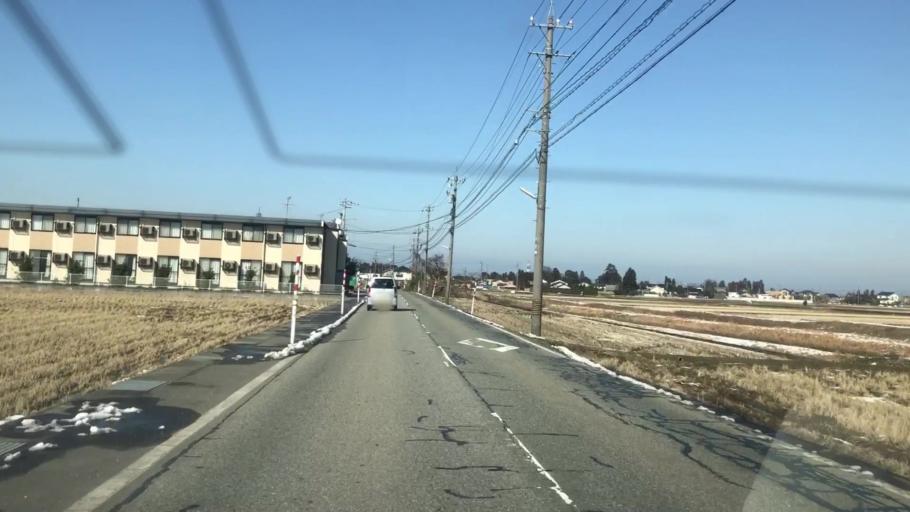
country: JP
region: Toyama
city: Toyama-shi
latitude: 36.6516
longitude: 137.2453
